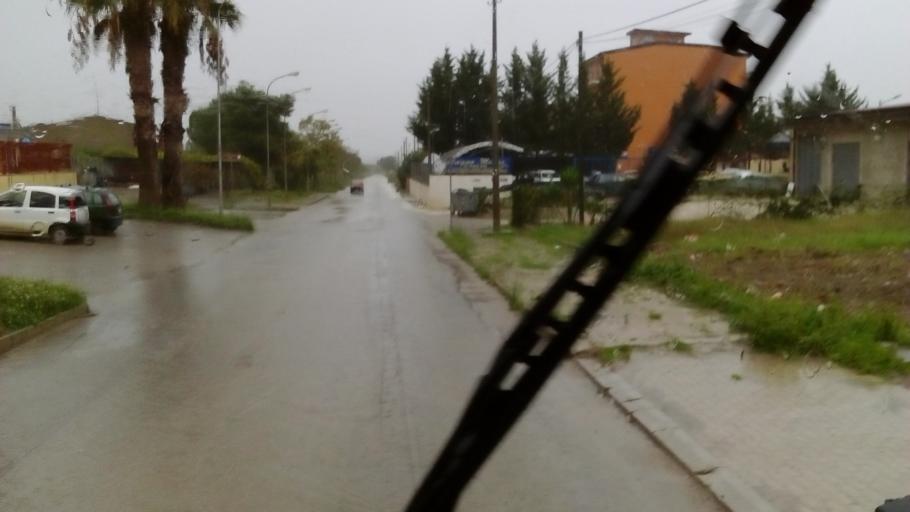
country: IT
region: Sicily
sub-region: Enna
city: Pietraperzia
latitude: 37.4137
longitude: 14.1421
